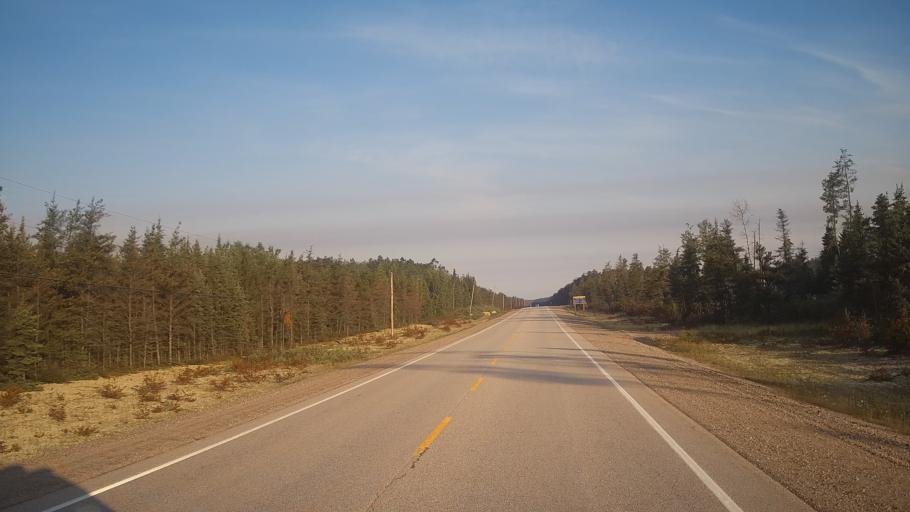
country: CA
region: Ontario
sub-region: Rainy River District
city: Atikokan
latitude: 49.2417
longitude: -91.0126
